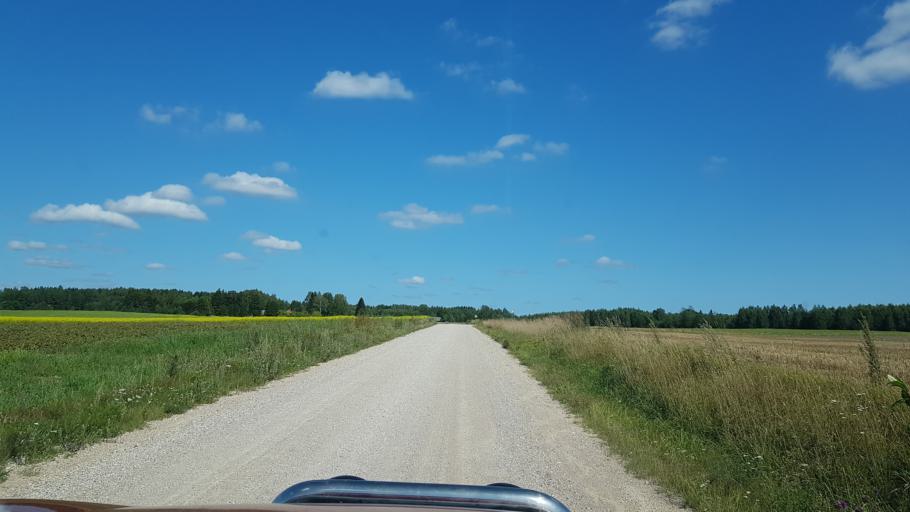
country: RU
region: Pskov
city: Pechory
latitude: 57.7133
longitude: 27.3966
